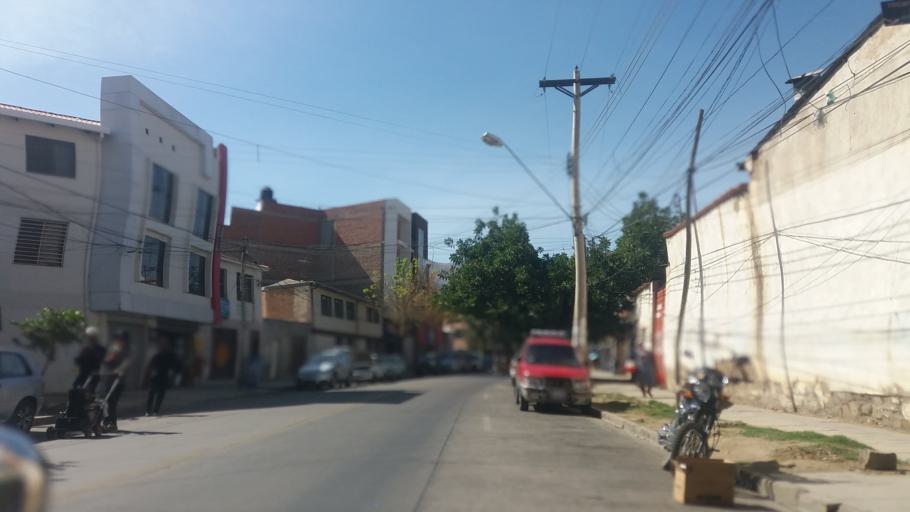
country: BO
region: Cochabamba
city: Cochabamba
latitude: -17.3982
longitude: -66.1635
